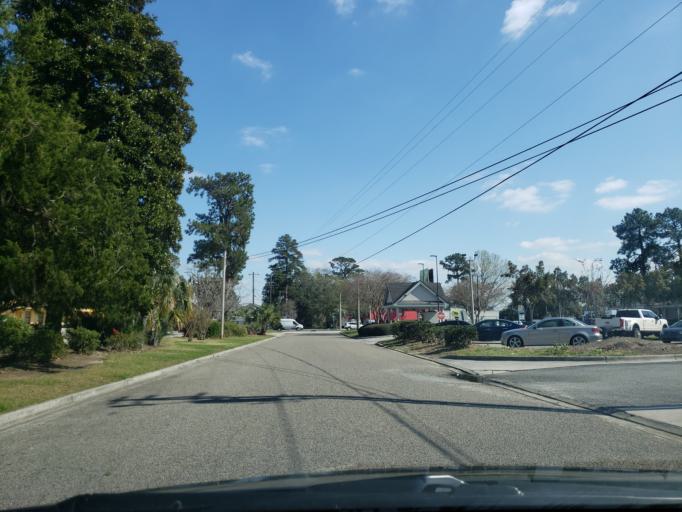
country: US
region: Georgia
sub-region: Chatham County
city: Isle of Hope
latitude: 32.0149
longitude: -81.1141
